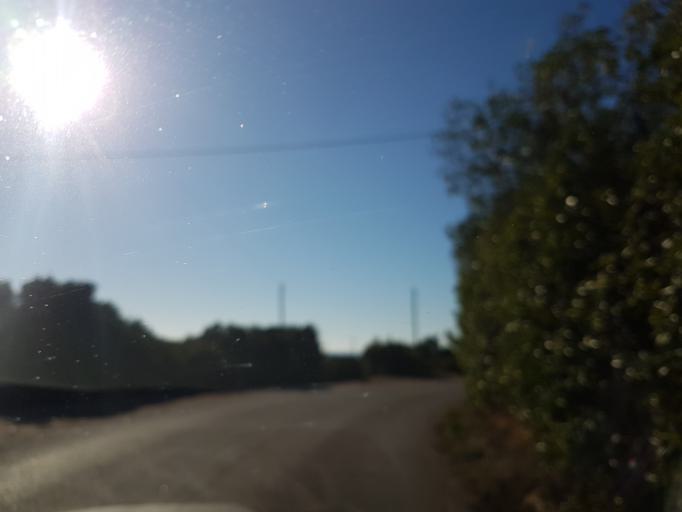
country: PT
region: Faro
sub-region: Lagoa
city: Carvoeiro
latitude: 37.0926
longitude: -8.4191
